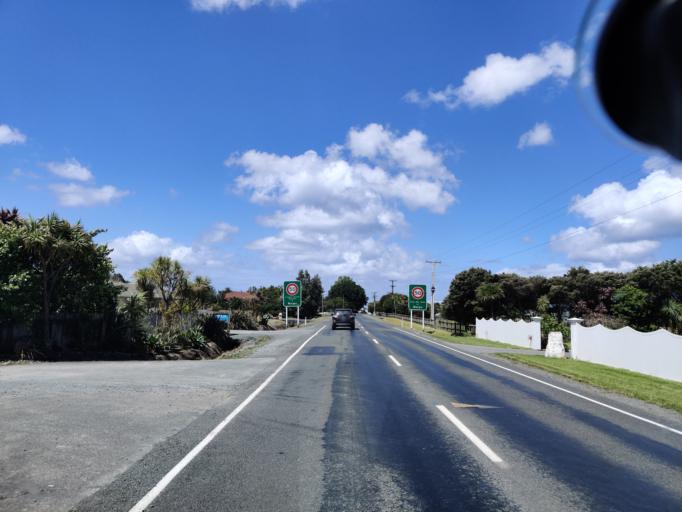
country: NZ
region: Northland
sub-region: Whangarei
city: Ruakaka
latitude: -35.9833
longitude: 174.4357
